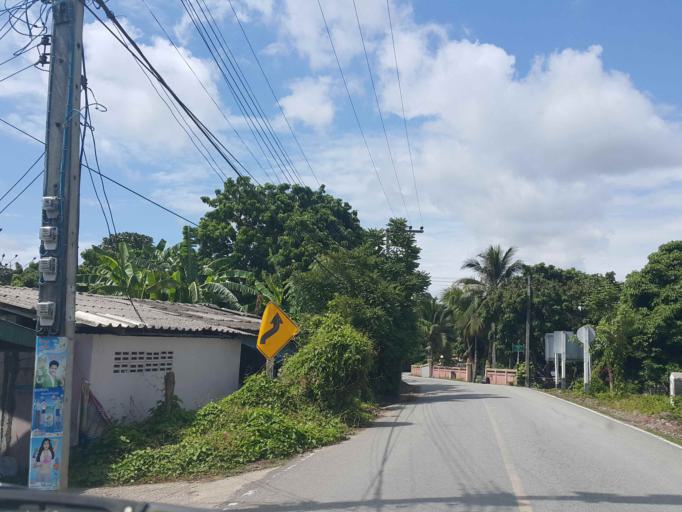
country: TH
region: Chiang Mai
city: Saraphi
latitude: 18.7369
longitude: 99.0501
